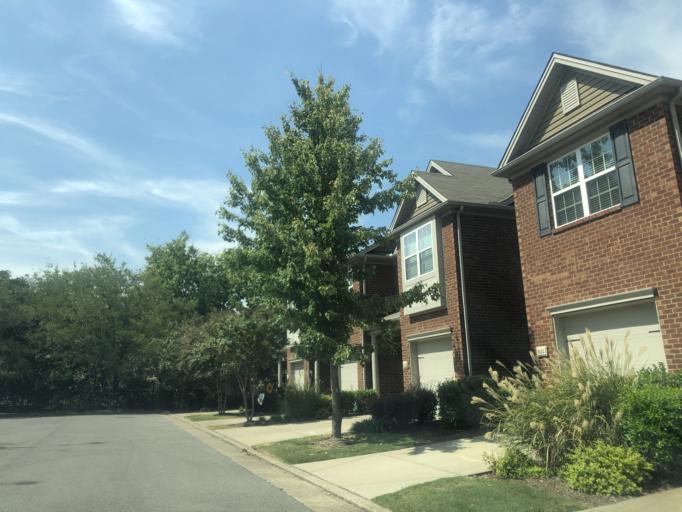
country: US
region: Tennessee
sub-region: Williamson County
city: Brentwood
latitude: 36.0564
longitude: -86.7381
